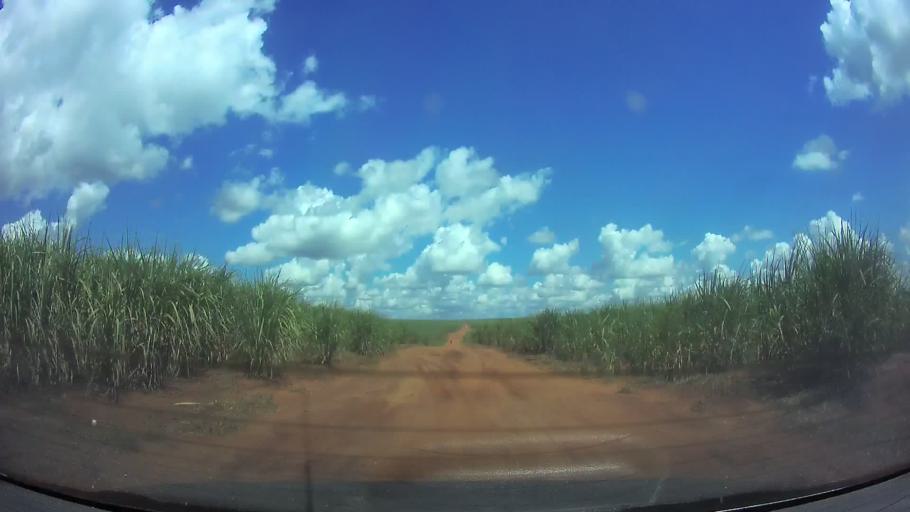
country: PY
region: Paraguari
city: La Colmena
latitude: -25.9556
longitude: -56.7659
